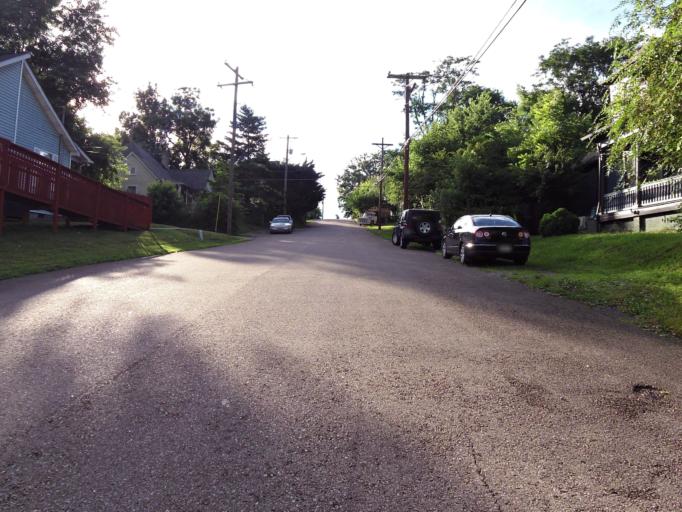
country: US
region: Tennessee
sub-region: Knox County
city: Knoxville
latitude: 35.9847
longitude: -83.9277
